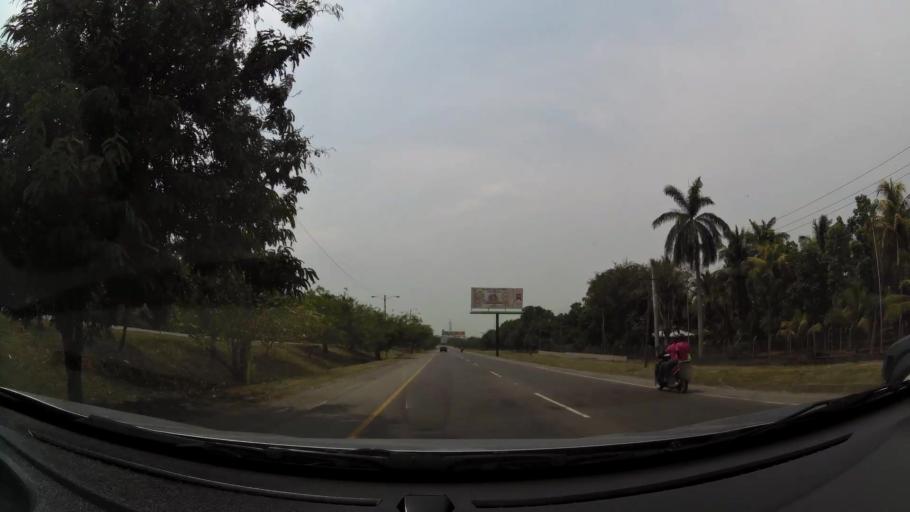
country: HN
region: Cortes
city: Nuevo Chamelecon
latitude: 15.3872
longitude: -87.9908
